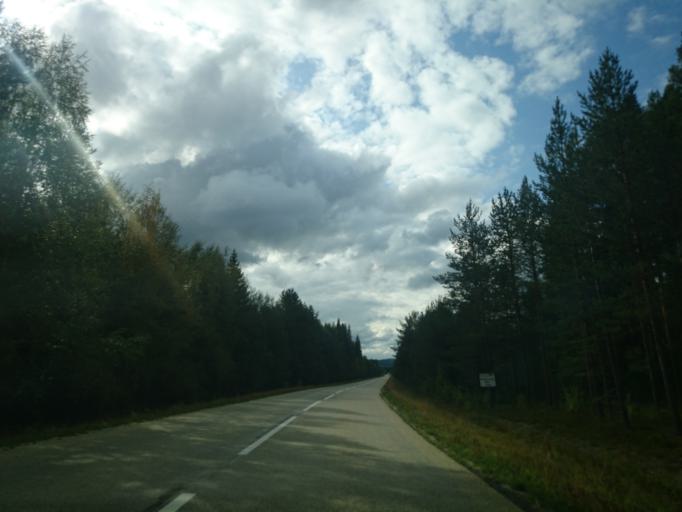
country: SE
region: Jaemtland
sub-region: Harjedalens Kommun
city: Sveg
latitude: 62.4117
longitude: 13.6113
